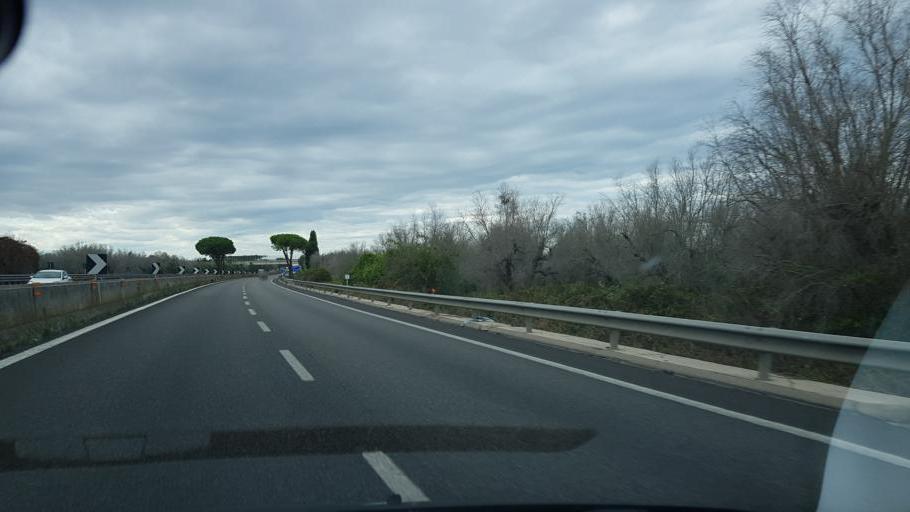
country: IT
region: Apulia
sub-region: Provincia di Lecce
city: Squinzano
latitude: 40.4529
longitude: 18.0658
